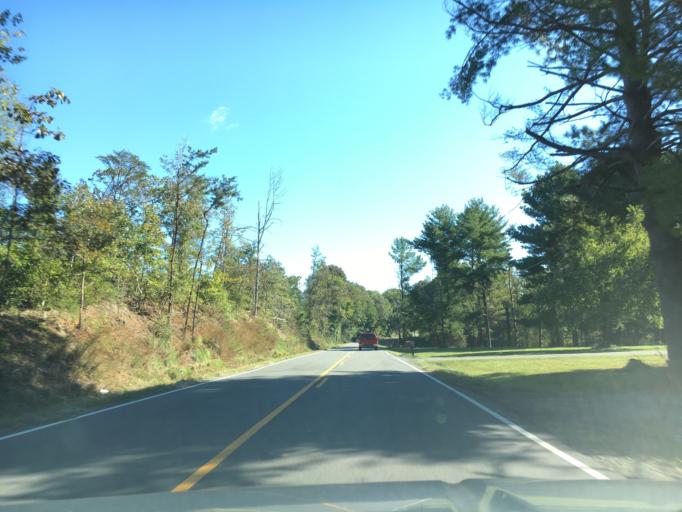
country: US
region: Virginia
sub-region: Goochland County
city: Goochland
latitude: 37.6975
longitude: -77.8658
